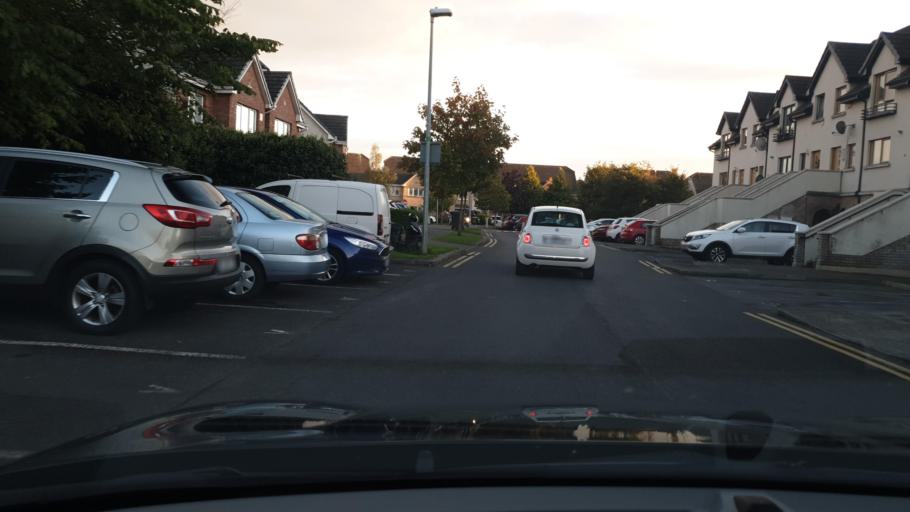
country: IE
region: Leinster
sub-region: An Mhi
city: Ashbourne
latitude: 53.5013
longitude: -6.3899
